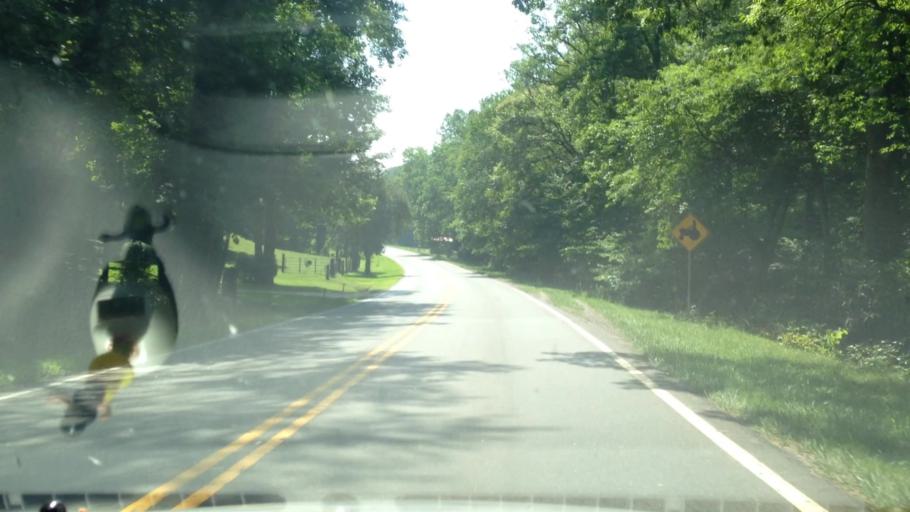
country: US
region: Virginia
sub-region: Patrick County
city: Stuart
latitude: 36.5884
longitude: -80.4079
